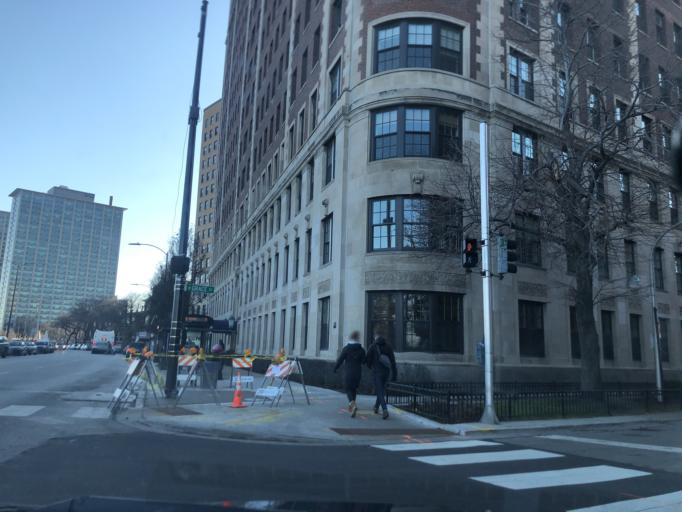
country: US
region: Illinois
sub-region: Cook County
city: Evanston
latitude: 41.9524
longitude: -87.6451
